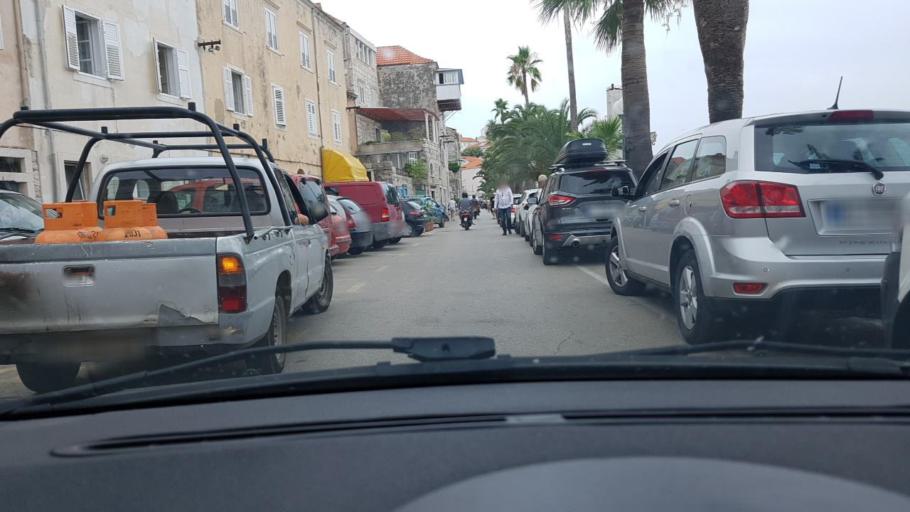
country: HR
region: Dubrovacko-Neretvanska
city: Korcula
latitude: 42.9608
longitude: 17.1337
